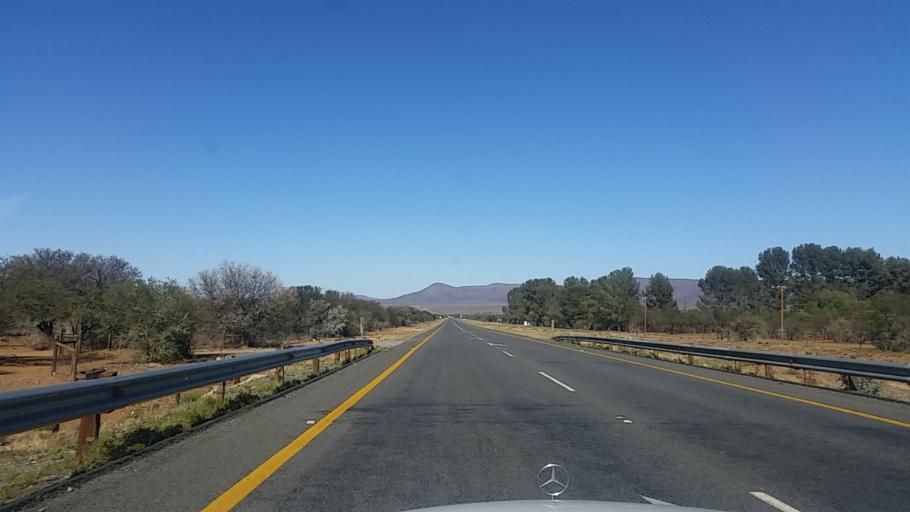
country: ZA
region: Eastern Cape
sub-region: Cacadu District Municipality
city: Graaff-Reinet
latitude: -31.9787
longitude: 24.7037
